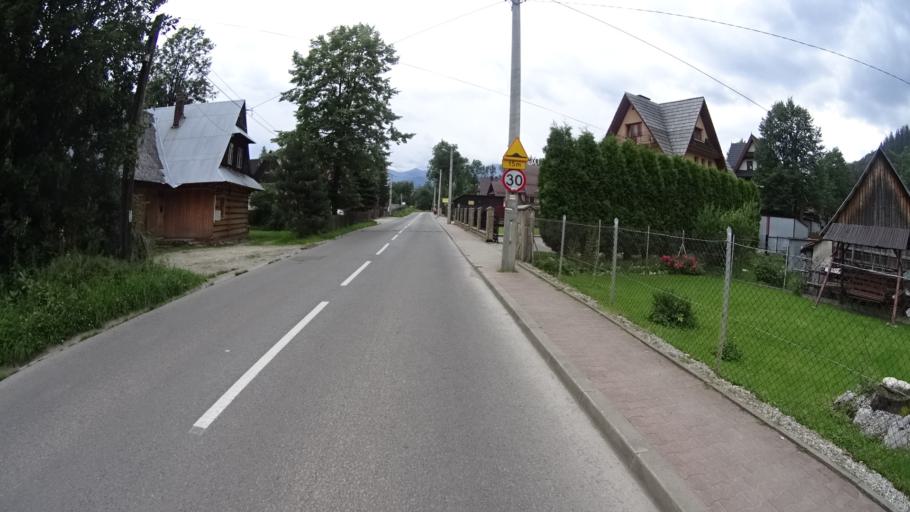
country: PL
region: Lesser Poland Voivodeship
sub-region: Powiat tatrzanski
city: Poronin
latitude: 49.3261
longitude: 19.9892
